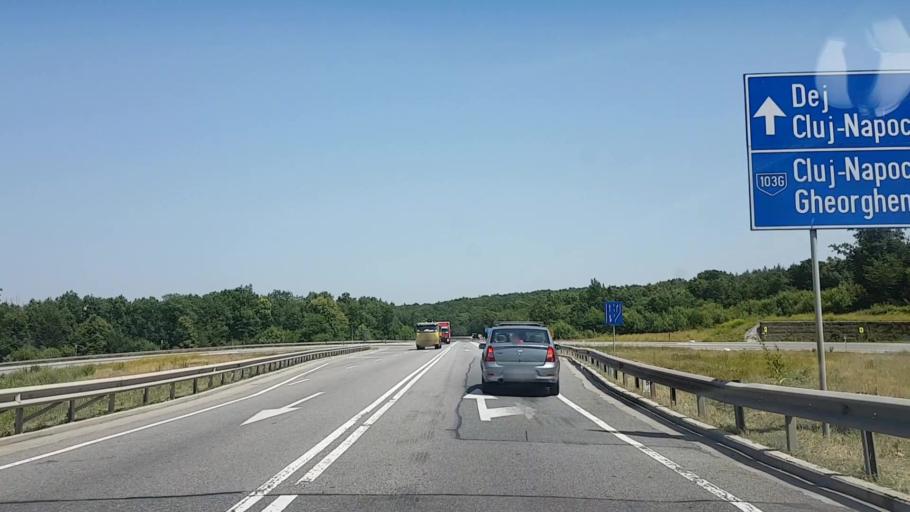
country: RO
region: Cluj
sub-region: Comuna Feleacu
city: Gheorghieni
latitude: 46.7282
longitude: 23.6600
